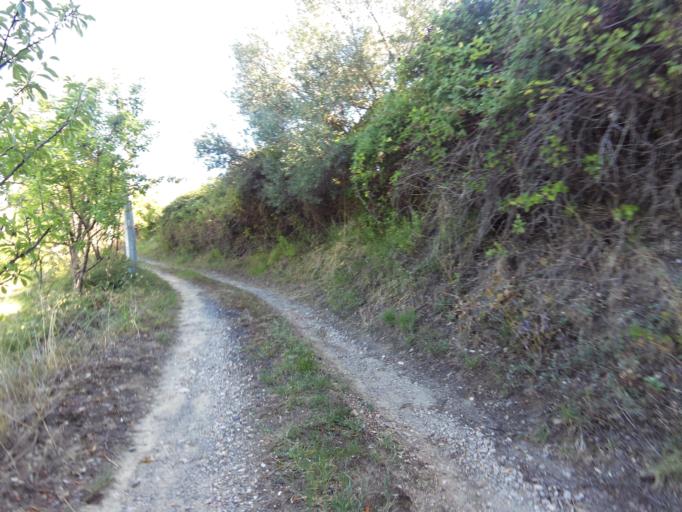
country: IT
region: Calabria
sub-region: Provincia di Reggio Calabria
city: Pazzano
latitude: 38.4518
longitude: 16.4545
